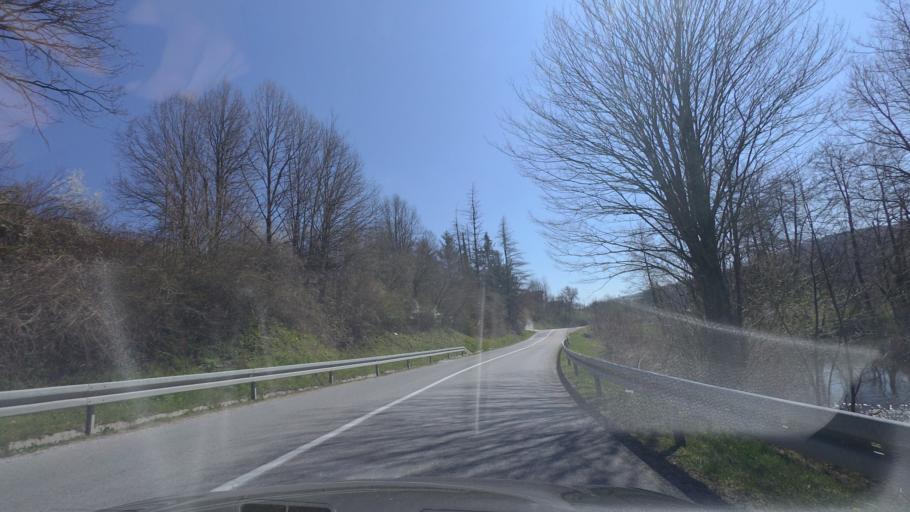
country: HR
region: Karlovacka
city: Vojnic
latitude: 45.3757
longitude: 15.6510
